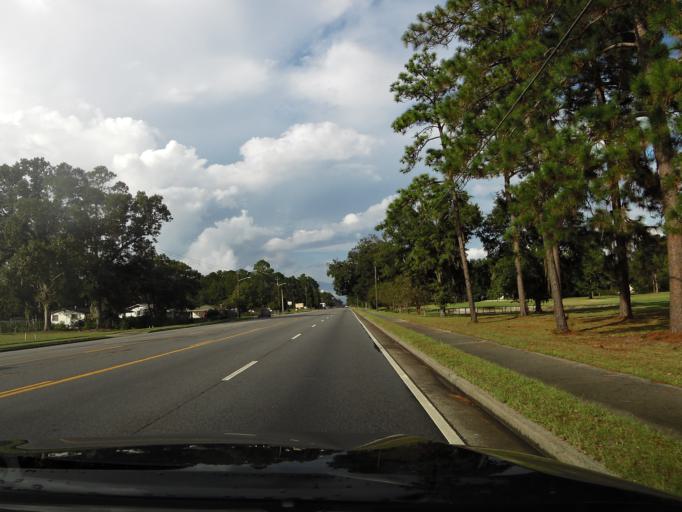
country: US
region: Georgia
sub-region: Liberty County
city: Walthourville
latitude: 31.7989
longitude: -81.6060
